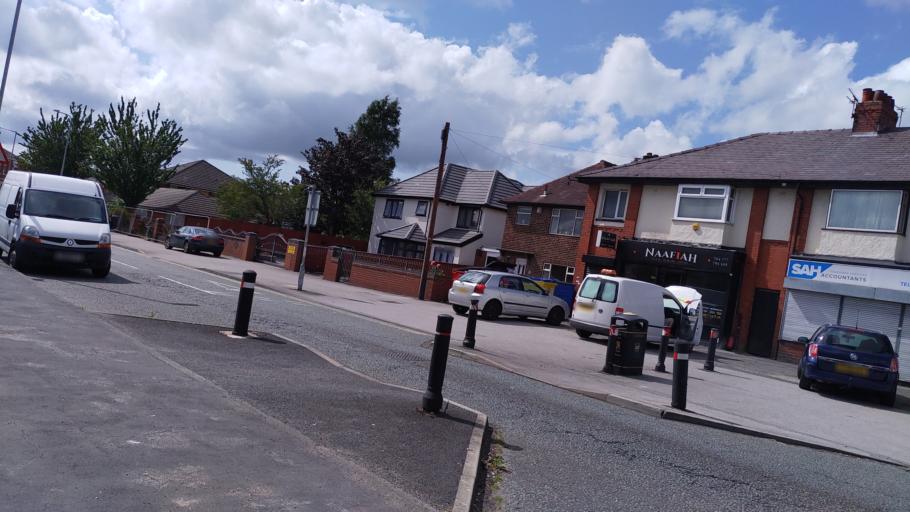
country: GB
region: England
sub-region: Lancashire
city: Preston
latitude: 53.7698
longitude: -2.6857
